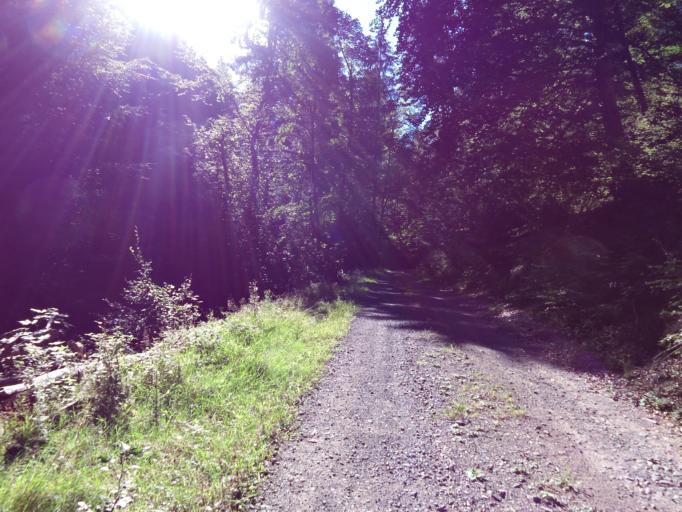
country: DE
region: Rheinland-Pfalz
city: Neidenfels
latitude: 49.4236
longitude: 8.0374
